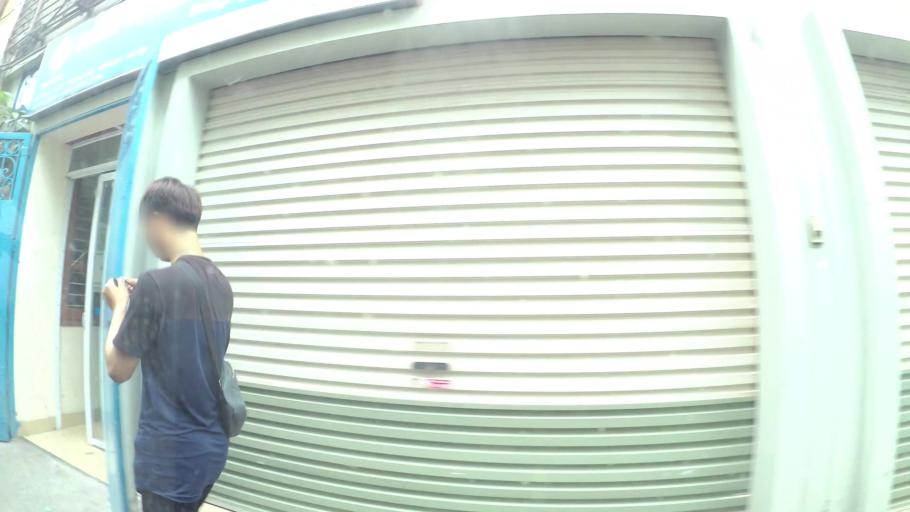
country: VN
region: Ha Noi
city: Dong Da
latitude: 21.0190
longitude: 105.8268
